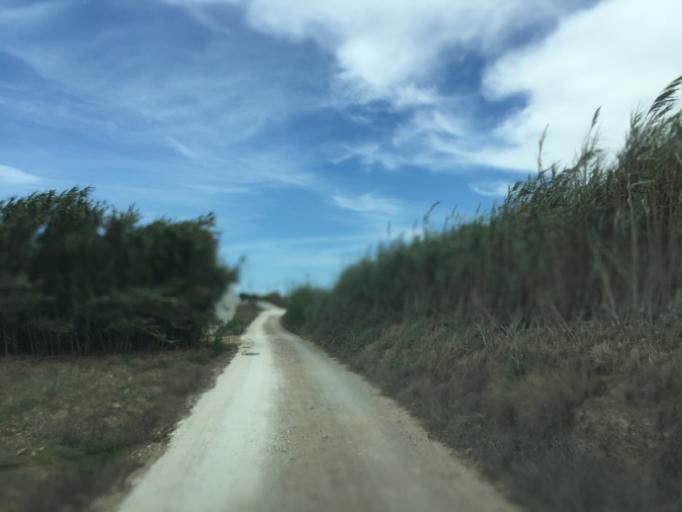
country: PT
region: Lisbon
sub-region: Lourinha
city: Lourinha
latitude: 39.1938
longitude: -9.3395
